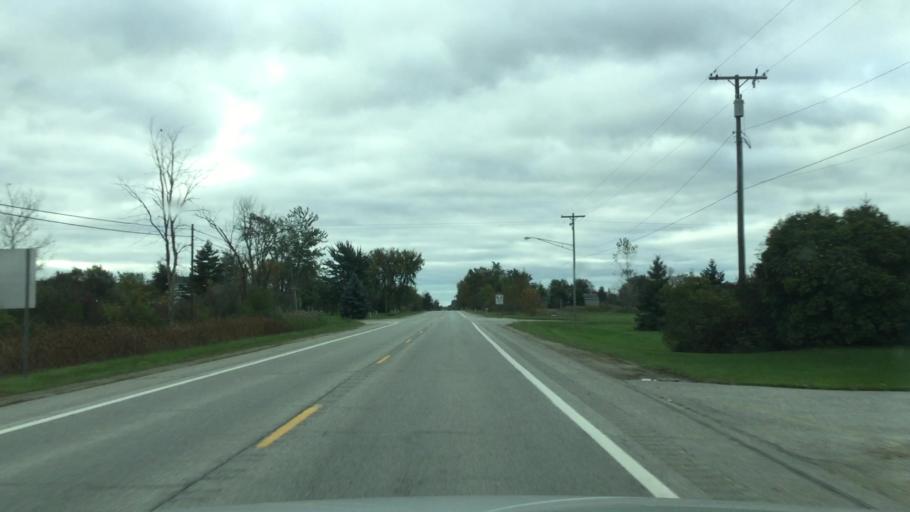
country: US
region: Michigan
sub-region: Macomb County
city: Memphis
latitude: 42.9563
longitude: -82.7633
